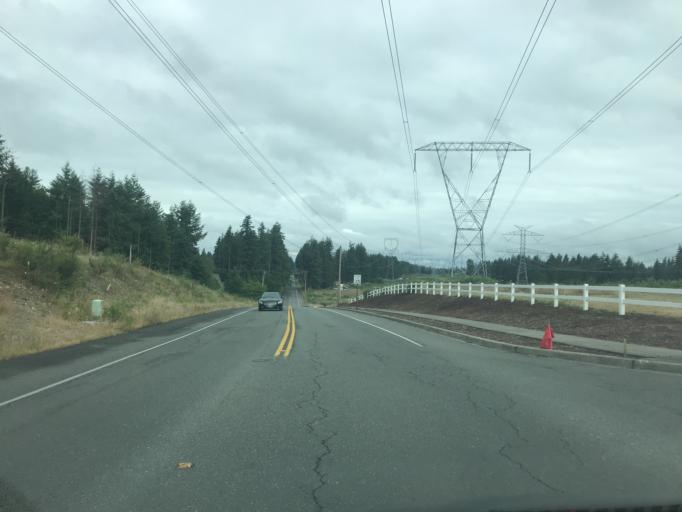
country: US
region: Washington
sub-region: King County
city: Ravensdale
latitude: 47.3435
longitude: -122.0217
